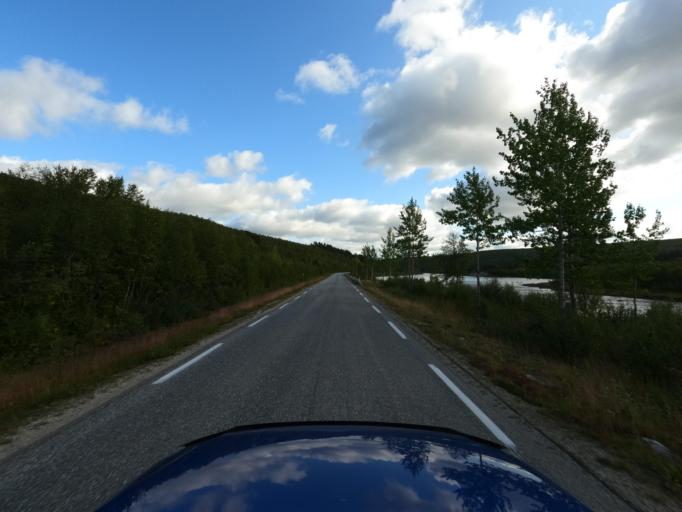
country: NO
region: Finnmark Fylke
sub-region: Porsanger
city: Lakselv
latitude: 69.4236
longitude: 24.8348
